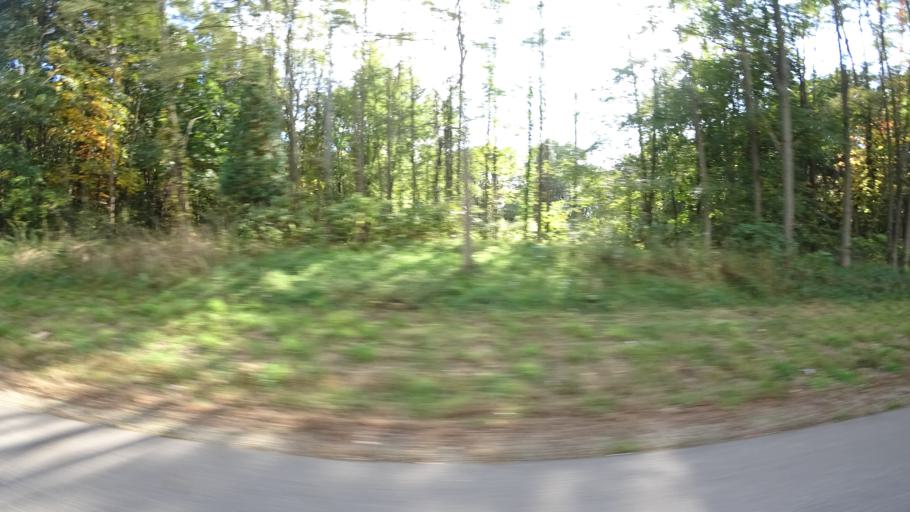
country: US
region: Michigan
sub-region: Saint Joseph County
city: Centreville
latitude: 41.9257
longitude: -85.5525
